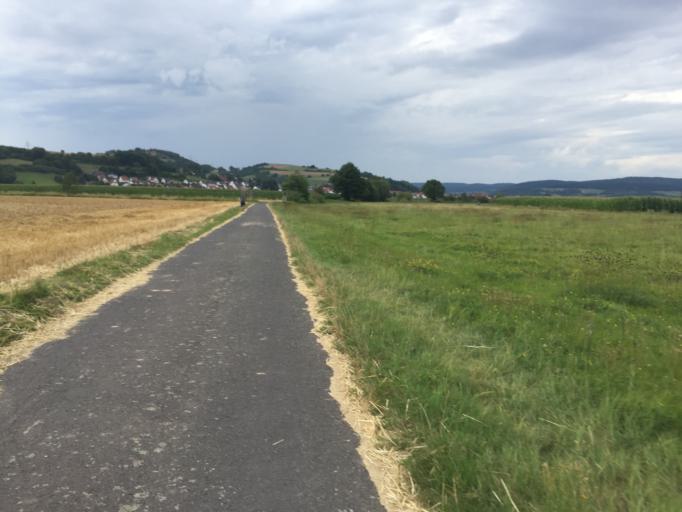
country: DE
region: Hesse
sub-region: Regierungsbezirk Kassel
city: Alheim
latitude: 51.0160
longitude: 9.6828
